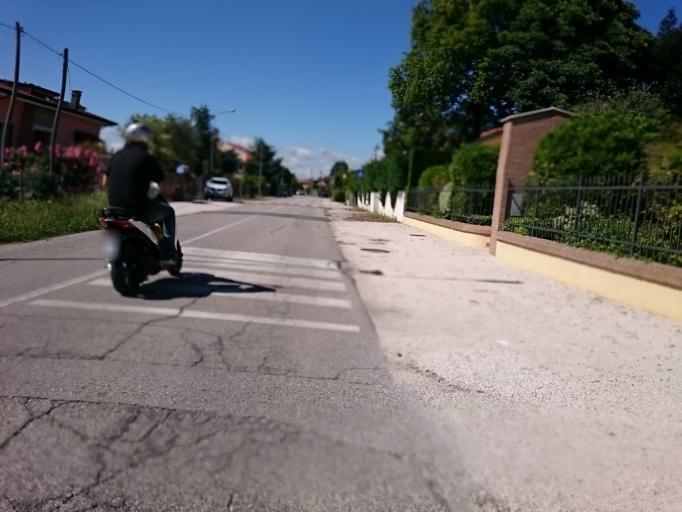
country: IT
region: Veneto
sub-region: Provincia di Padova
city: Piove di Sacco-Piovega
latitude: 45.2890
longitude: 12.0410
